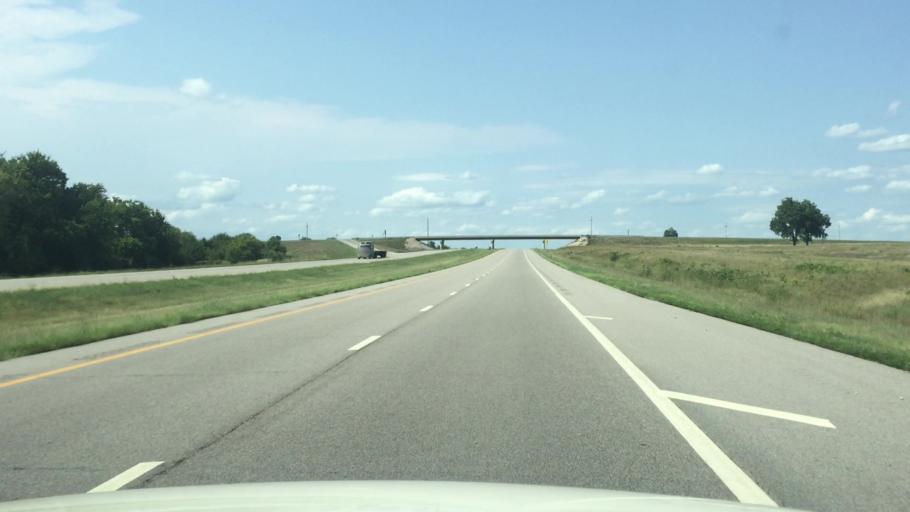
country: US
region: Kansas
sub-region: Linn County
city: La Cygne
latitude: 38.3987
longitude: -94.6876
